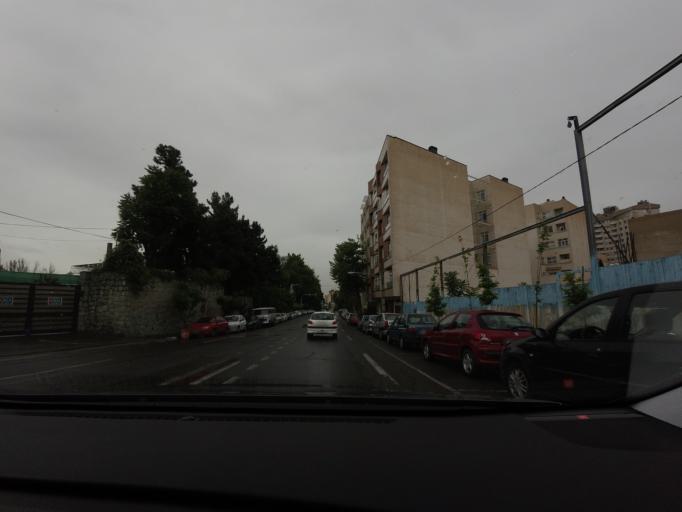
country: IR
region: Tehran
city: Tajrish
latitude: 35.7689
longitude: 51.4000
